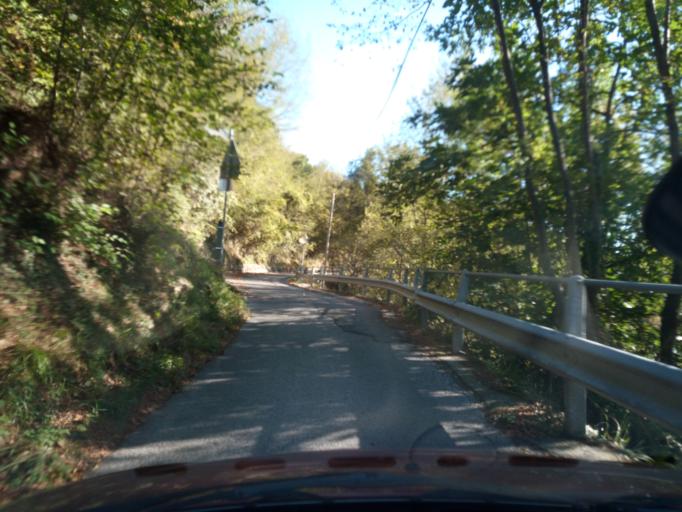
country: IT
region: Liguria
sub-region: Provincia di Genova
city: Isoverde
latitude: 44.4913
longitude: 8.8457
